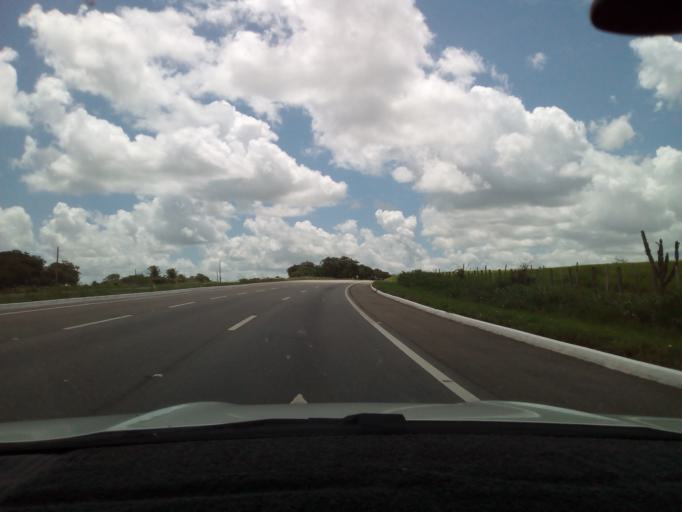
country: BR
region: Paraiba
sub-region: Pilar
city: Pilar
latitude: -7.1882
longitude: -35.2128
